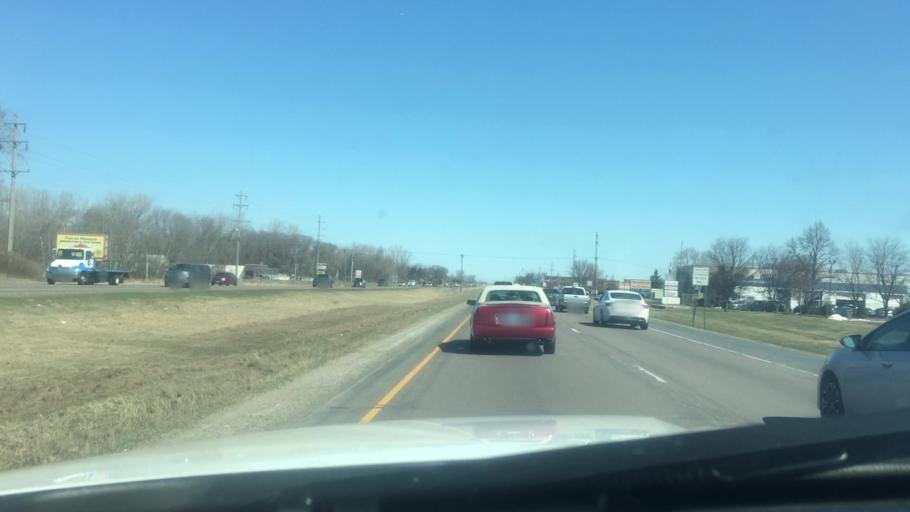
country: US
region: Minnesota
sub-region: Anoka County
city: Blaine
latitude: 45.1514
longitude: -93.2350
